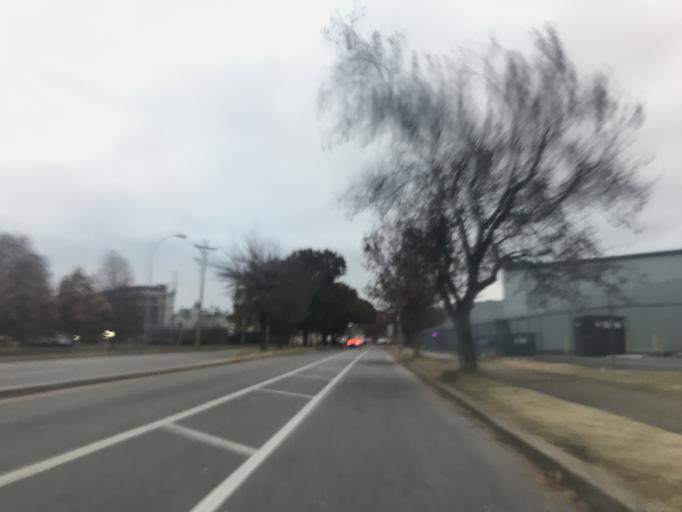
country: US
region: Kentucky
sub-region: Jefferson County
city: Louisville
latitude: 38.2493
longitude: -85.7725
